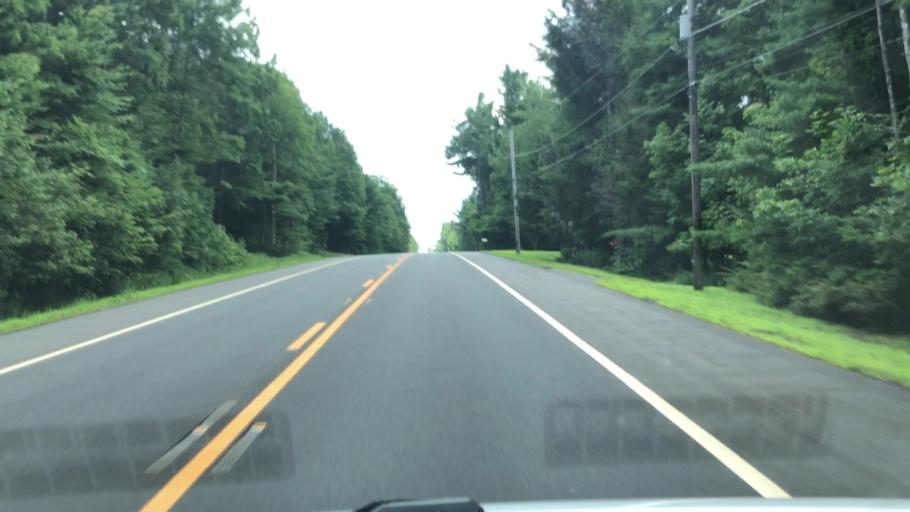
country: US
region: Massachusetts
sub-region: Franklin County
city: Ashfield
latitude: 42.4891
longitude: -72.8092
